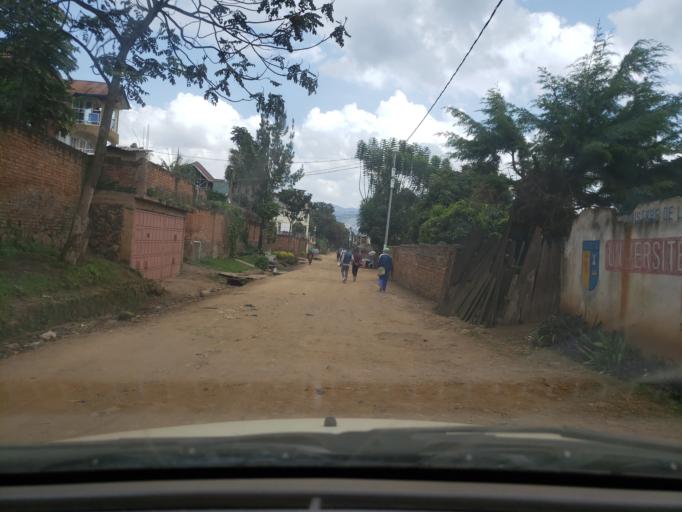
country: RW
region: Western Province
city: Cyangugu
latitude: -2.4965
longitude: 28.8868
